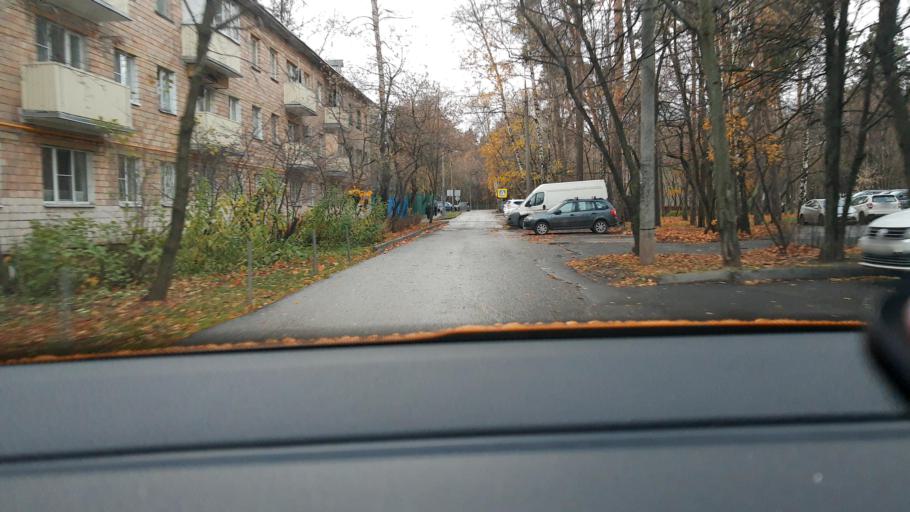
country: RU
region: Moscow
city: Vatutino
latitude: 55.8866
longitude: 37.7030
